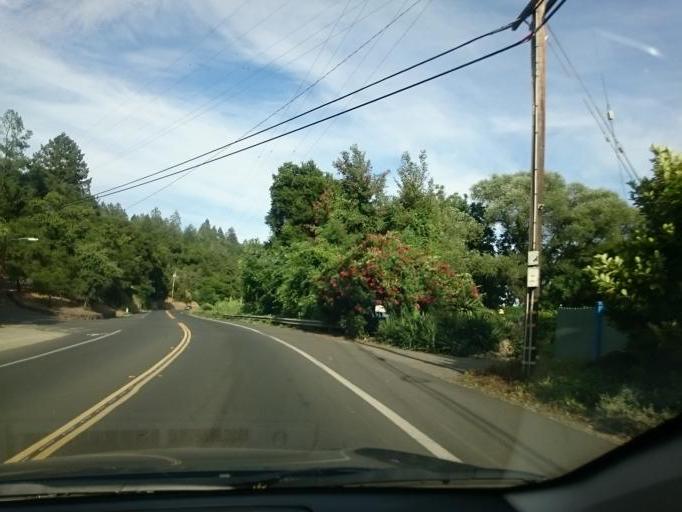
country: US
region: California
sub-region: Napa County
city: Deer Park
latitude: 38.5196
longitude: -122.4705
